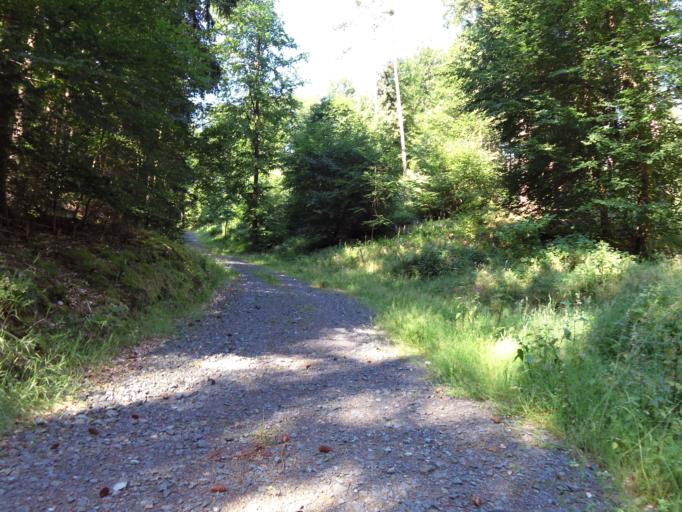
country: DE
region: Rheinland-Pfalz
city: Weidenthal
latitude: 49.4478
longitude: 8.0173
